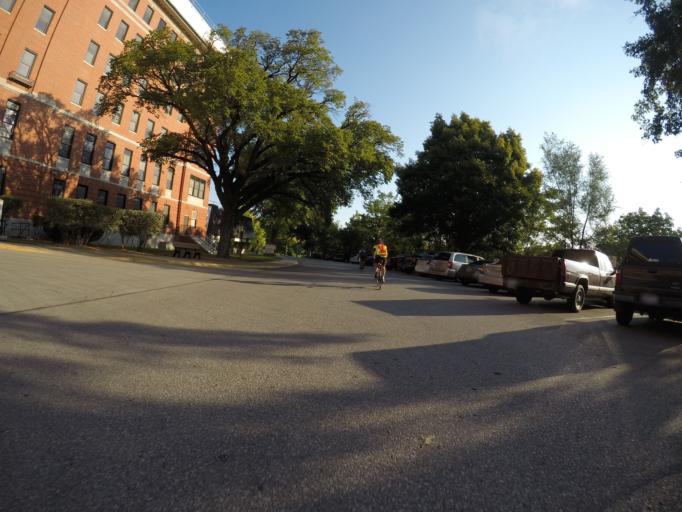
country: US
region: Kansas
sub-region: Leavenworth County
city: Lansing
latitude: 39.2823
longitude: -94.8959
